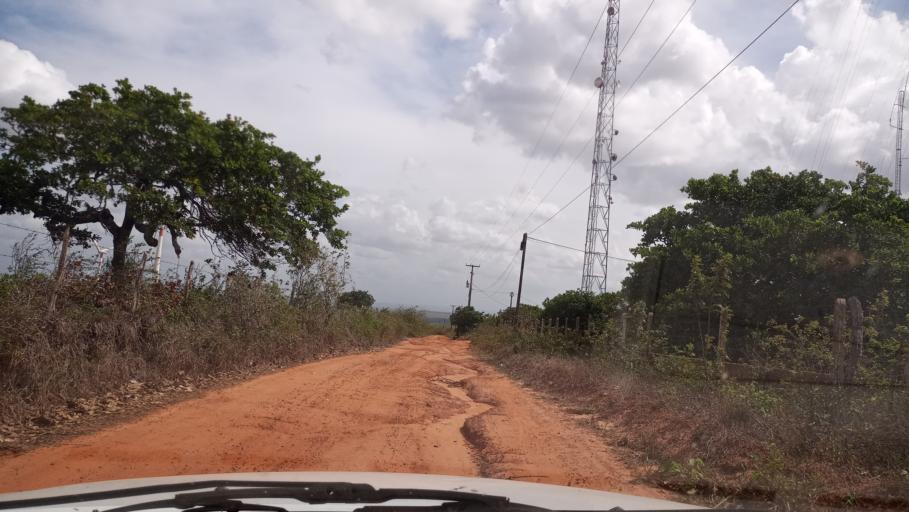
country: BR
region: Rio Grande do Norte
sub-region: Joao Camara
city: Joao Camara
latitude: -5.4176
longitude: -35.8565
